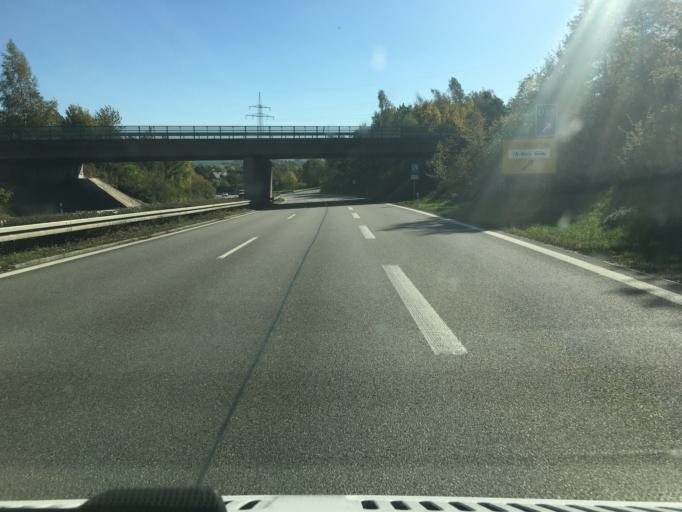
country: DE
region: Saxony
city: Dennheritz
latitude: 50.7890
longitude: 12.4758
